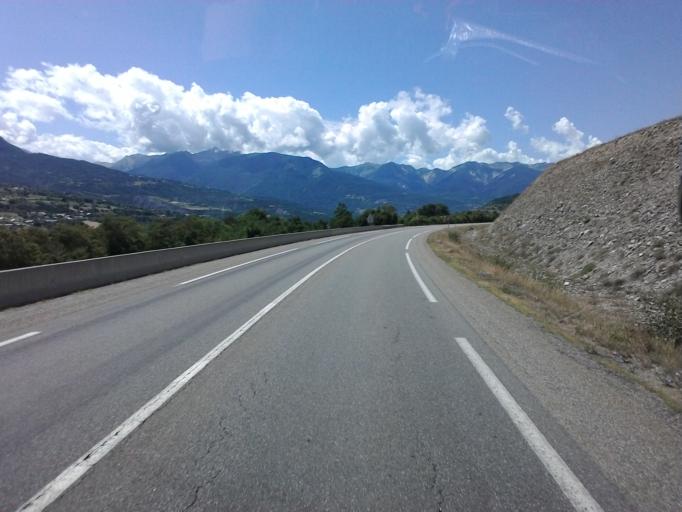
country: FR
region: Provence-Alpes-Cote d'Azur
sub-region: Departement des Hautes-Alpes
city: Embrun
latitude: 44.5989
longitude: 6.5249
